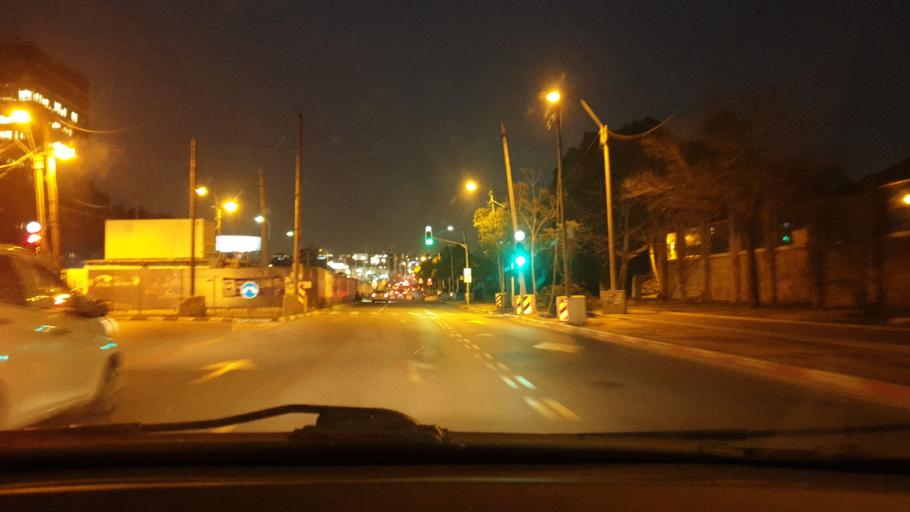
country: IL
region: Tel Aviv
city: Giv`at Shemu'el
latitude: 32.0925
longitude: 34.8496
